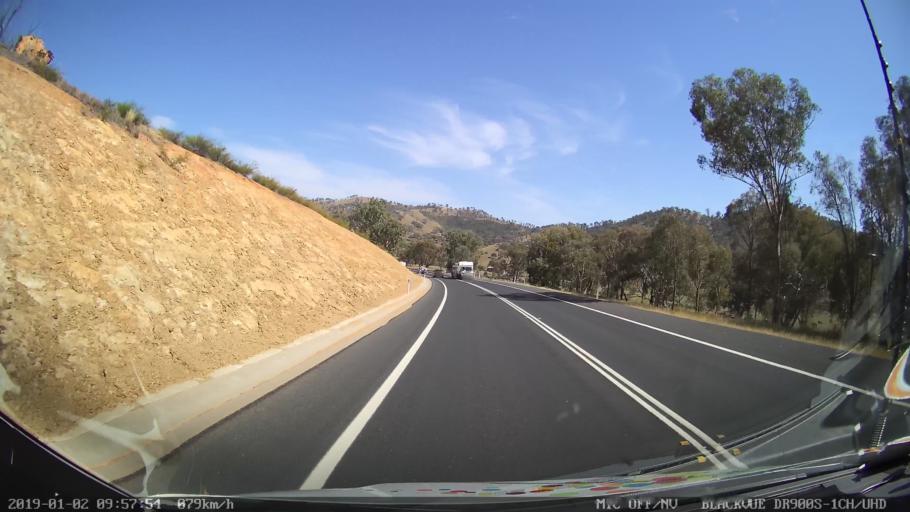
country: AU
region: New South Wales
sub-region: Tumut Shire
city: Tumut
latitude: -35.2001
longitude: 148.1644
